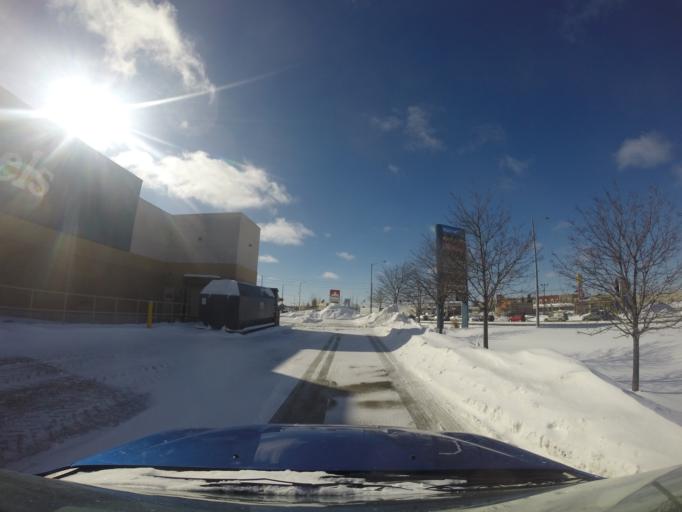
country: CA
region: Ontario
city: Cambridge
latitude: 43.4094
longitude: -80.3279
